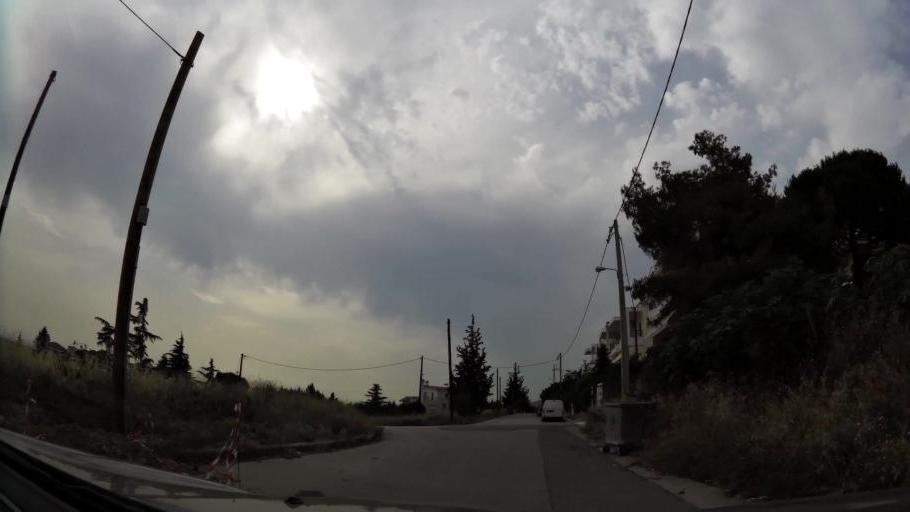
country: GR
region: Central Macedonia
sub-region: Nomos Thessalonikis
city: Oraiokastro
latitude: 40.7114
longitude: 22.9244
